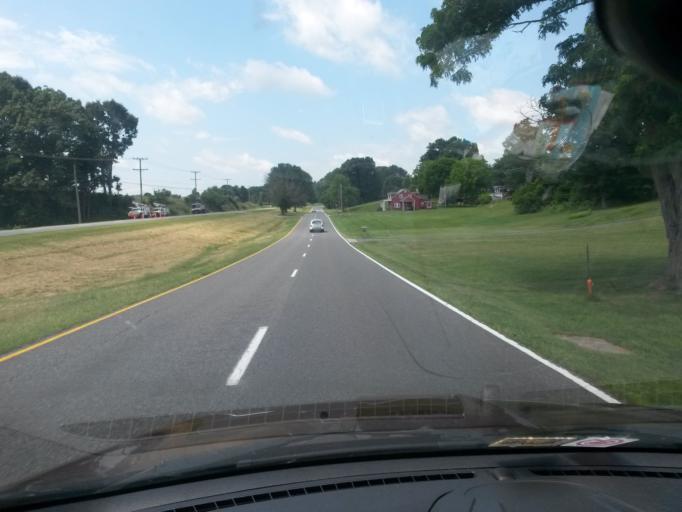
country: US
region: Virginia
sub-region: City of Buena Vista
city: Buena Vista
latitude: 37.9036
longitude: -79.2431
